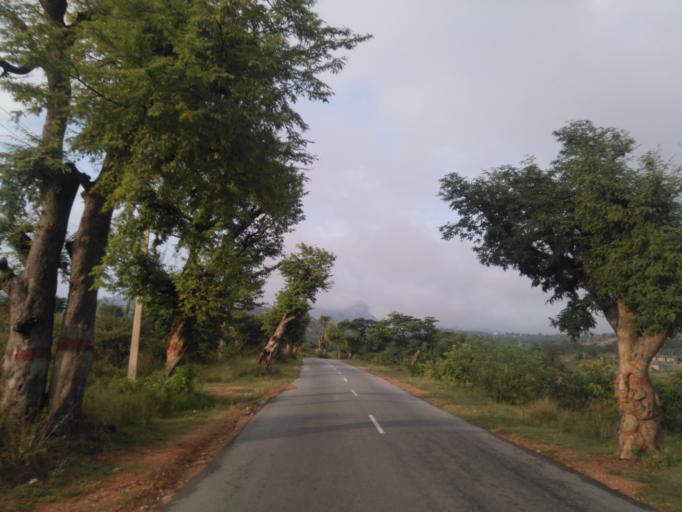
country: IN
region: Karnataka
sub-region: Ramanagara
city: Kanakapura
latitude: 12.5008
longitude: 77.3853
